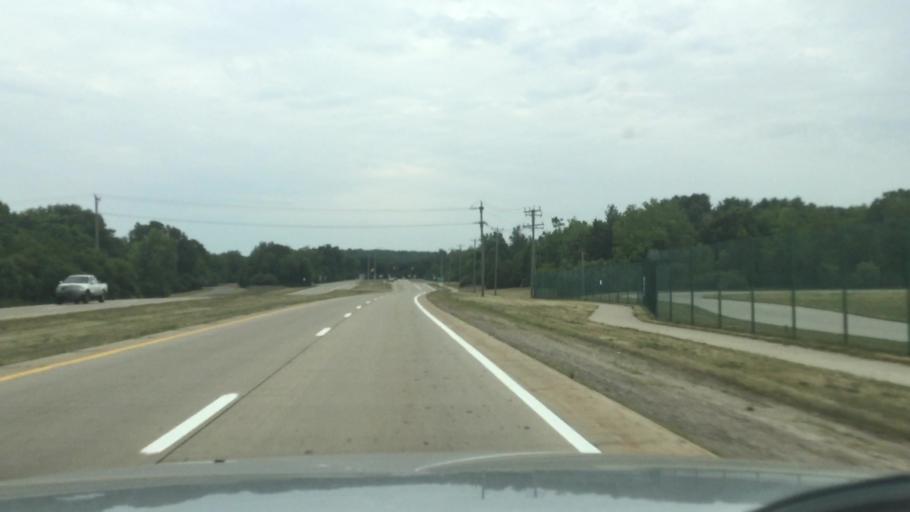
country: US
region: Michigan
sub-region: Oakland County
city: Waterford
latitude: 42.6660
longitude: -83.4385
